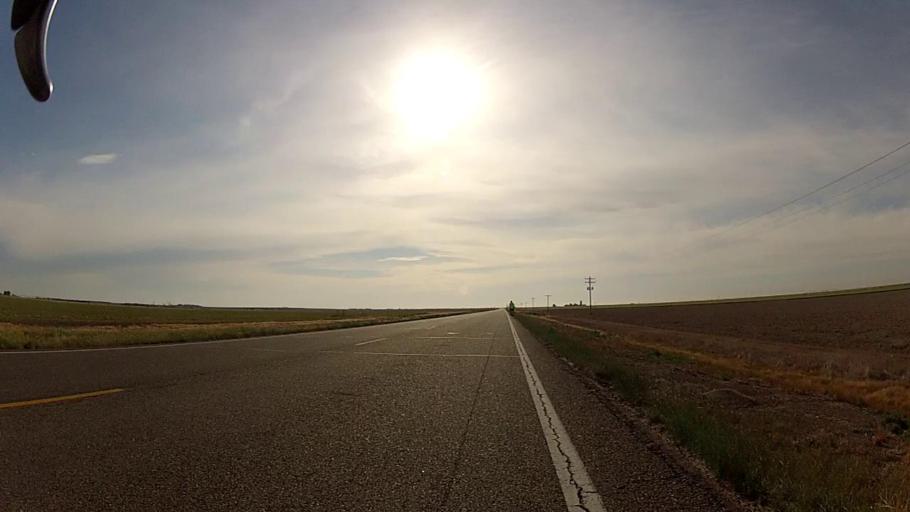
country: US
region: Kansas
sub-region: Grant County
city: Ulysses
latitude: 37.5766
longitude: -101.4639
